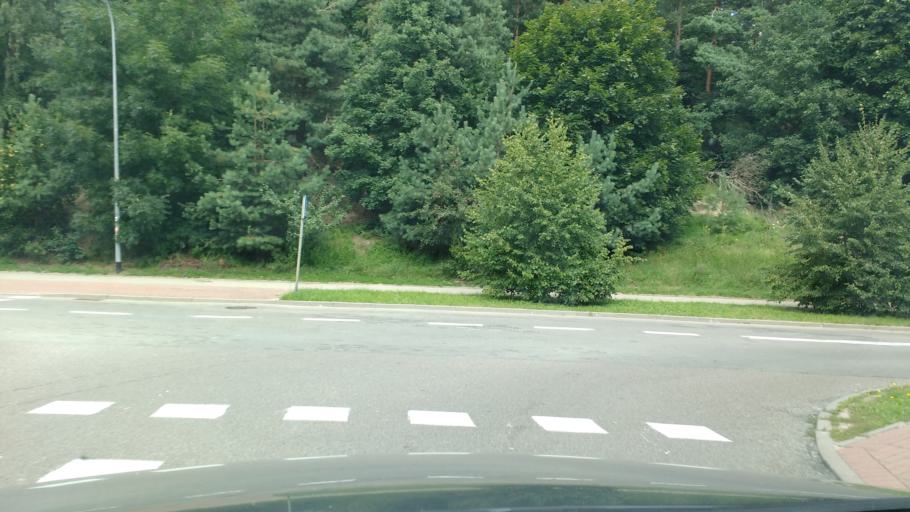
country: PL
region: Pomeranian Voivodeship
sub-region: Gdynia
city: Wielki Kack
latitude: 54.4690
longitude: 18.4830
